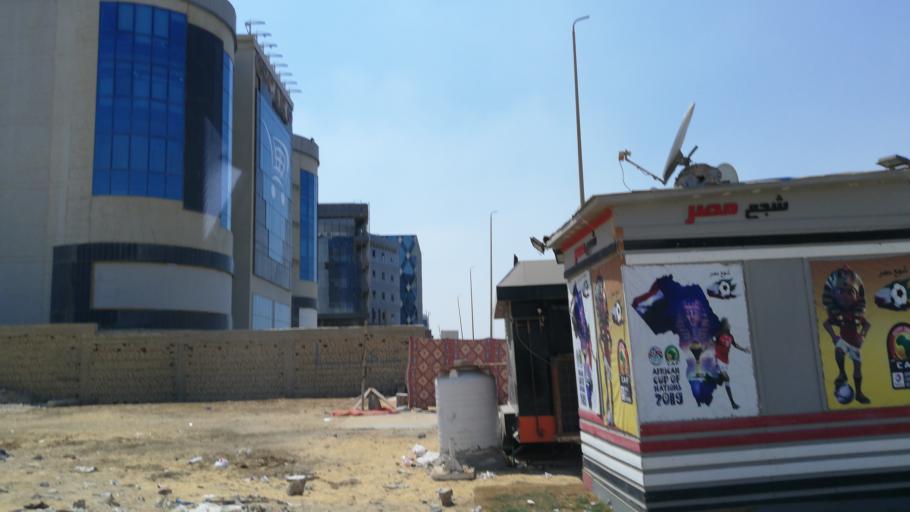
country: EG
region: Muhafazat al Qalyubiyah
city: Al Khankah
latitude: 30.0284
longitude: 31.4894
